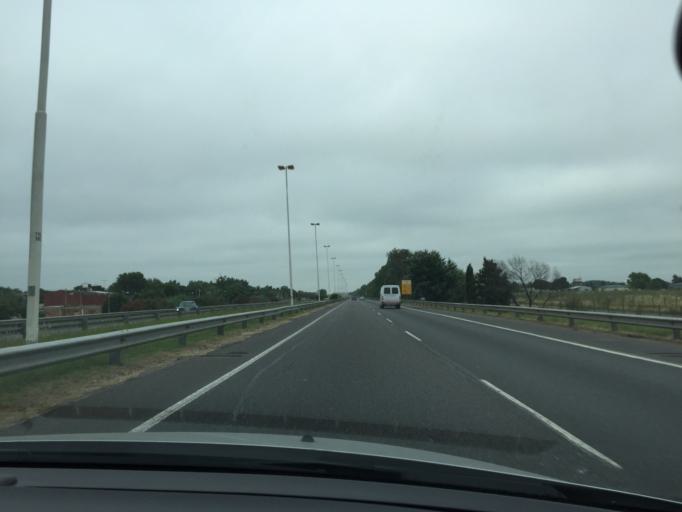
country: AR
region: Buenos Aires
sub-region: Partido de Ezeiza
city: Ezeiza
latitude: -34.8426
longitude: -58.5299
